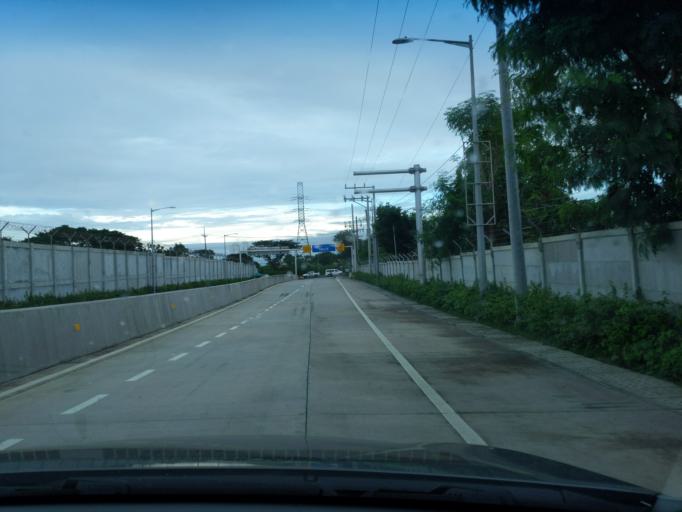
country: PH
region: Calabarzon
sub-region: Province of Cavite
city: Puting Kahoy
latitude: 14.2295
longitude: 121.0491
